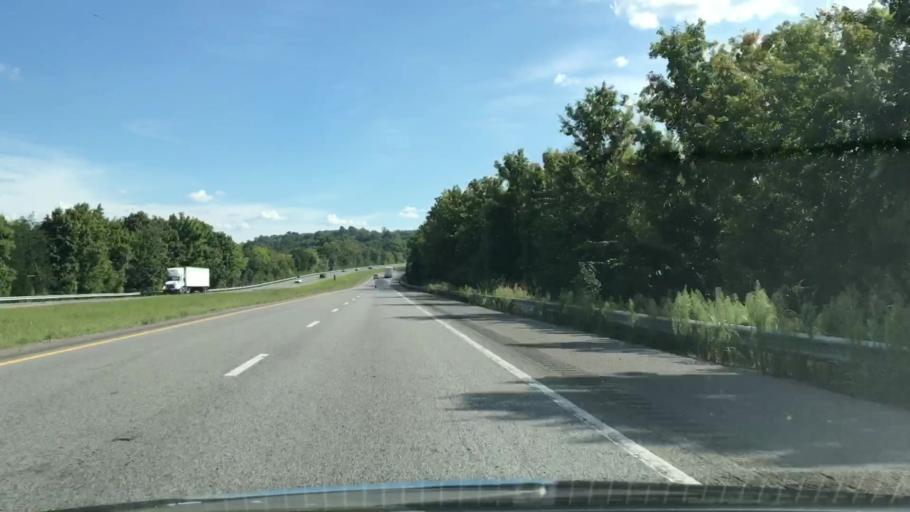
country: US
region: Alabama
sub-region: Limestone County
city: Ardmore
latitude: 35.1296
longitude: -86.8776
